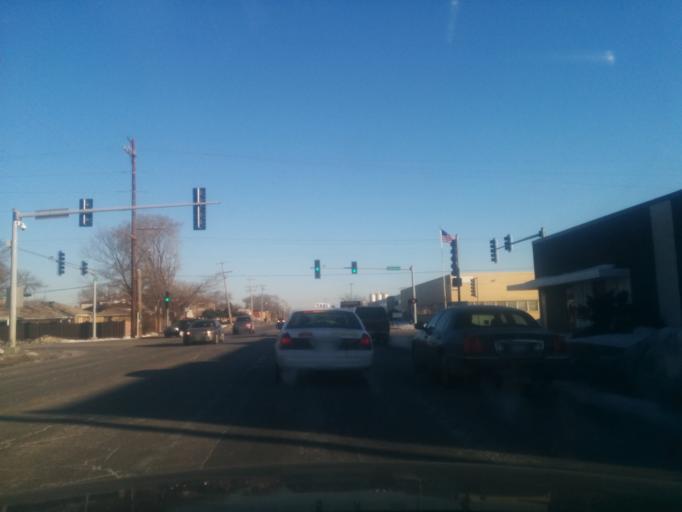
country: US
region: Illinois
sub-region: Cook County
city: Franklin Park
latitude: 41.9219
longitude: -87.8649
